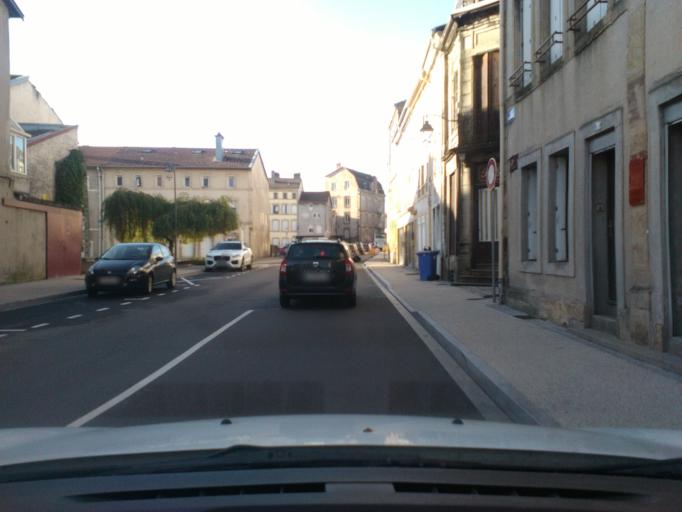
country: FR
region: Lorraine
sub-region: Departement des Vosges
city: Rambervillers
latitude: 48.3472
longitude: 6.6357
